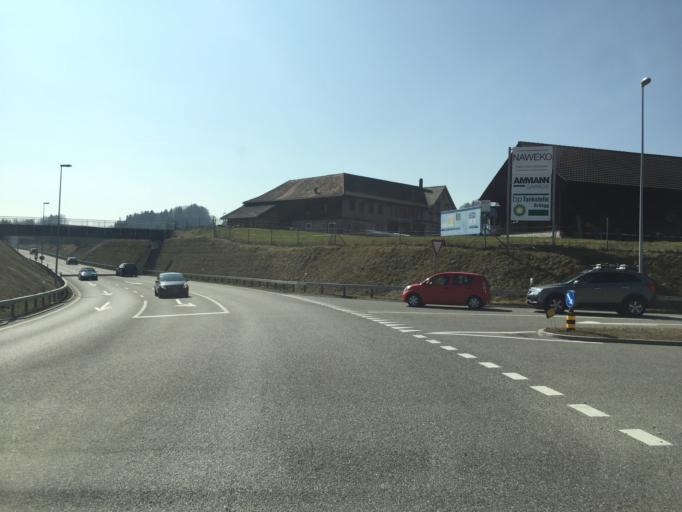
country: CH
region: Saint Gallen
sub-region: Wahlkreis Toggenburg
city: Lutisburg
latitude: 47.4056
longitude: 9.0693
